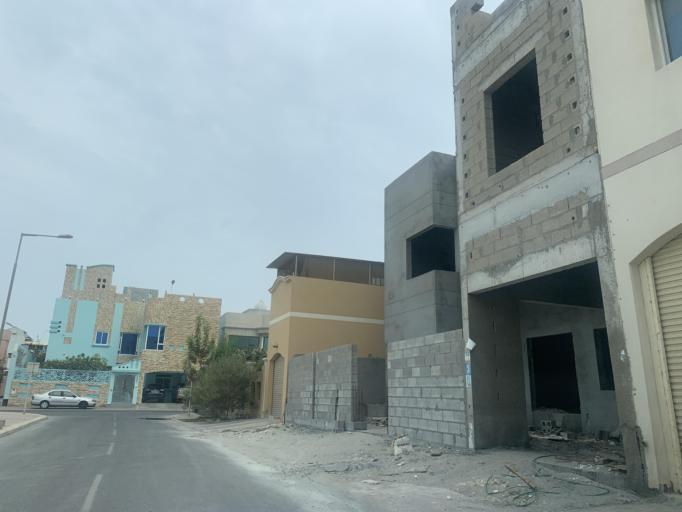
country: BH
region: Muharraq
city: Al Muharraq
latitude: 26.2848
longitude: 50.6365
